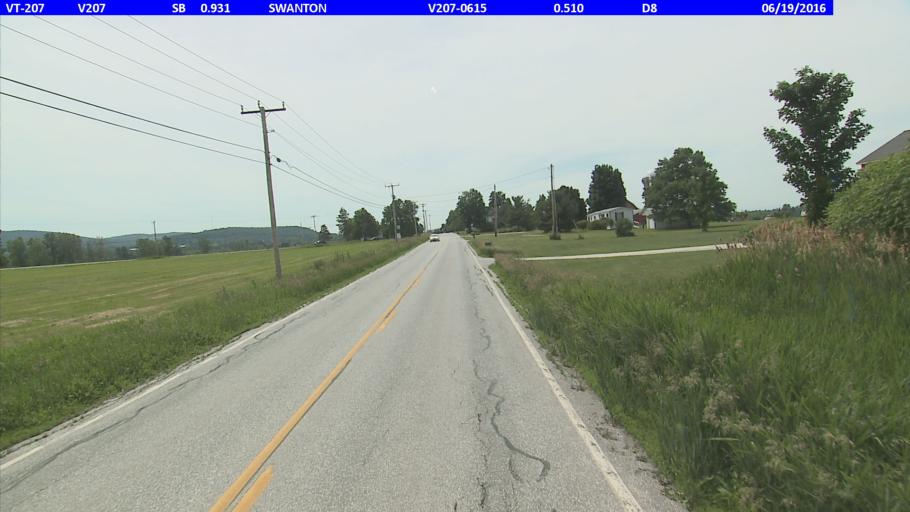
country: US
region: Vermont
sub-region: Franklin County
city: Saint Albans
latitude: 44.8523
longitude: -73.0756
